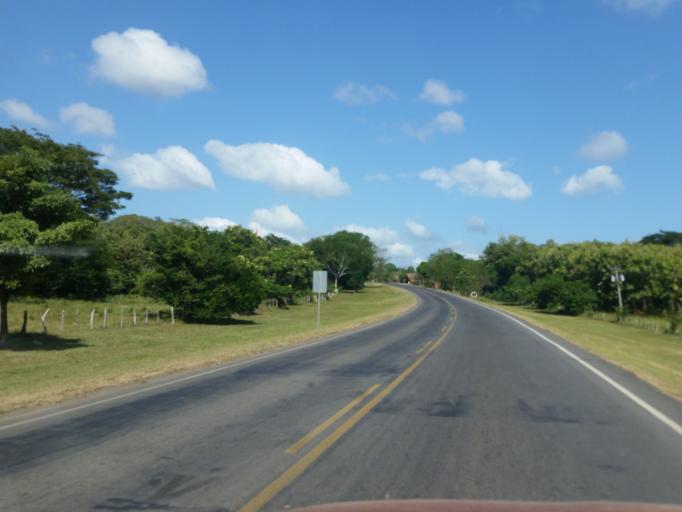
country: NI
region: Granada
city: Nandaime
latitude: 11.7232
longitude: -86.0123
